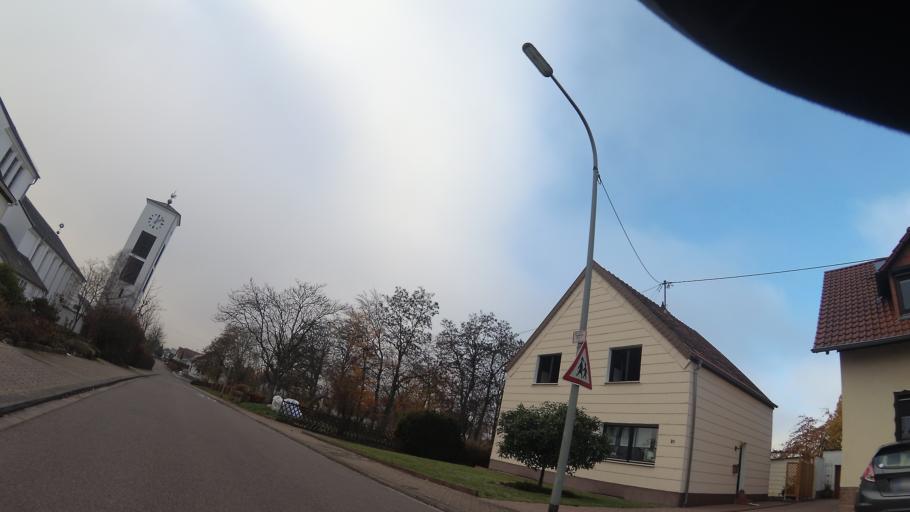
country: DE
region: Saarland
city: Schwalbach
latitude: 49.2993
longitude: 6.8043
